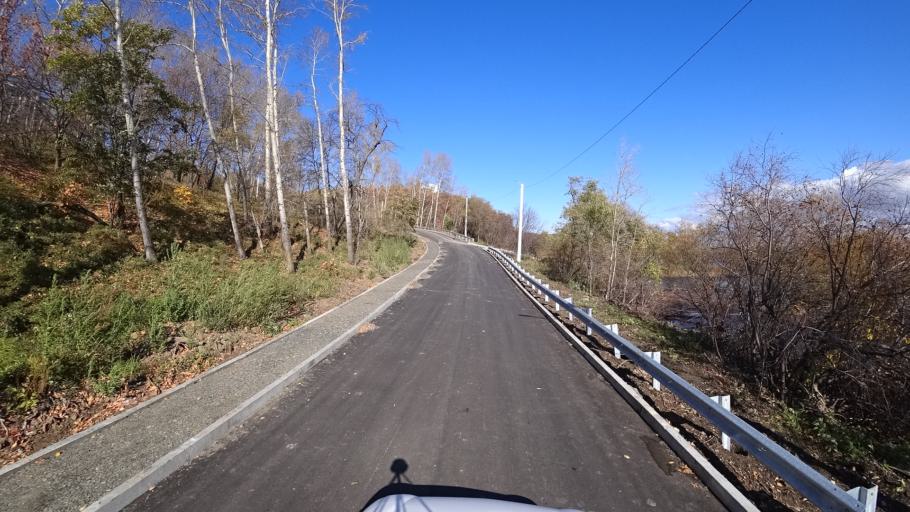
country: RU
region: Khabarovsk Krai
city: Amursk
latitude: 50.2156
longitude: 136.9071
